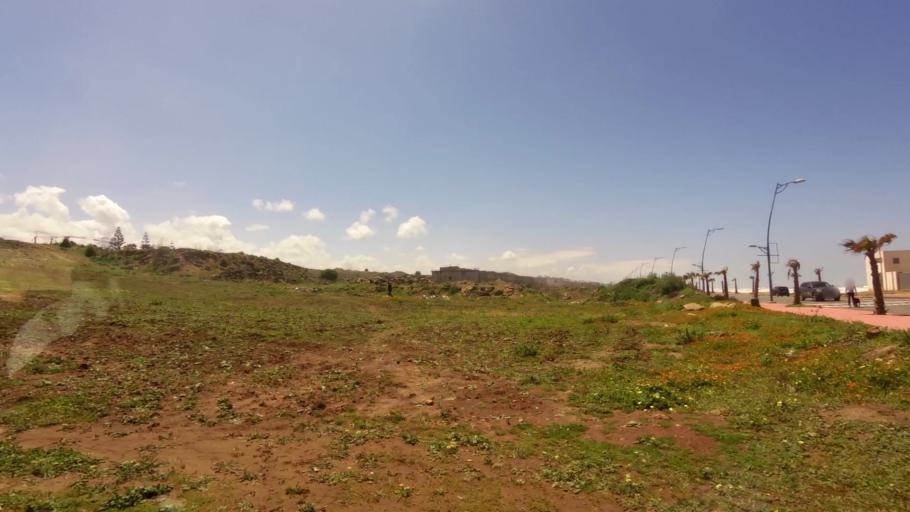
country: MA
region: Grand Casablanca
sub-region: Nouaceur
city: Dar Bouazza
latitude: 33.5260
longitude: -7.8370
